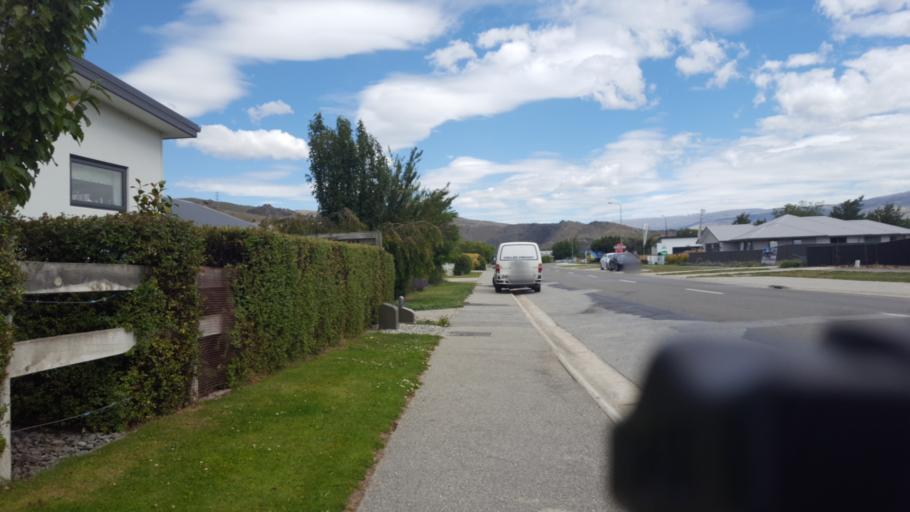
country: NZ
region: Otago
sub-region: Queenstown-Lakes District
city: Wanaka
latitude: -45.0380
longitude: 169.2160
